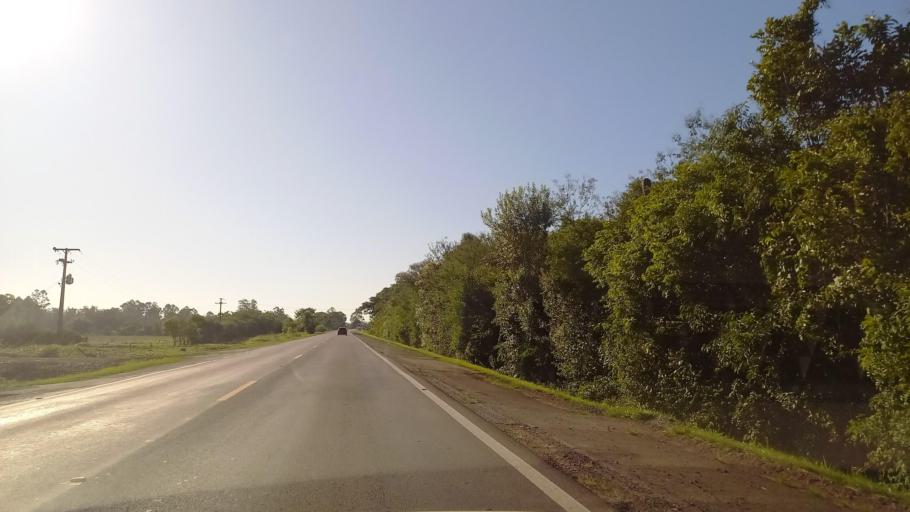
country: BR
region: Rio Grande do Sul
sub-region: Venancio Aires
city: Venancio Aires
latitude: -29.6690
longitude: -52.0345
